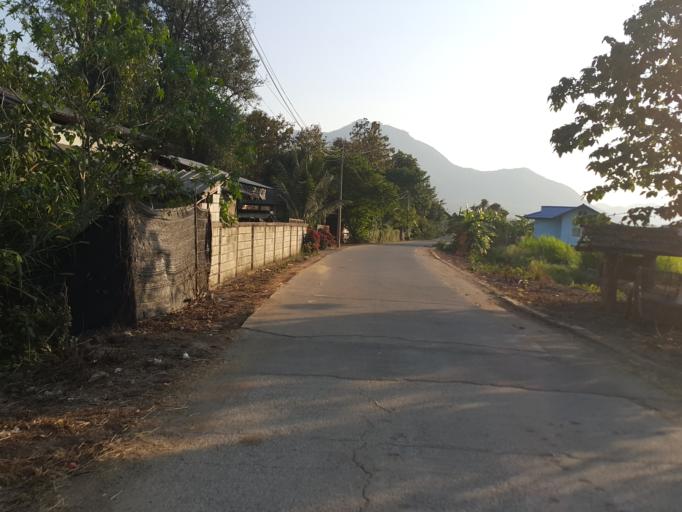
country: TH
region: Chiang Mai
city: Mae On
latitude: 18.7602
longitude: 99.2574
